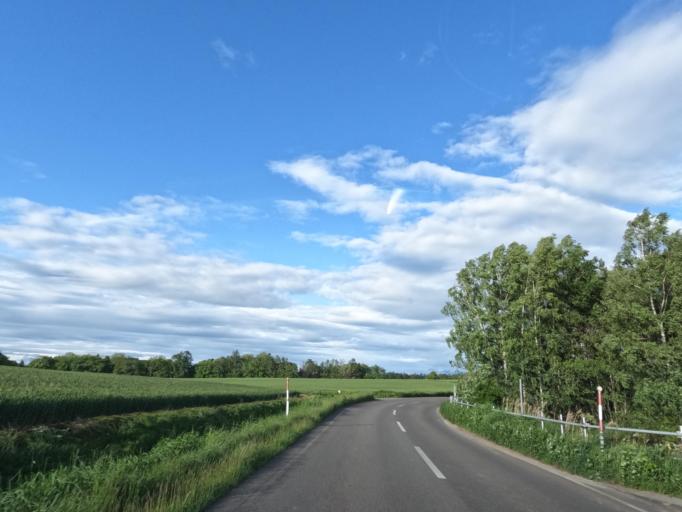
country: JP
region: Hokkaido
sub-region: Asahikawa-shi
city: Asahikawa
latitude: 43.6242
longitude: 142.4410
